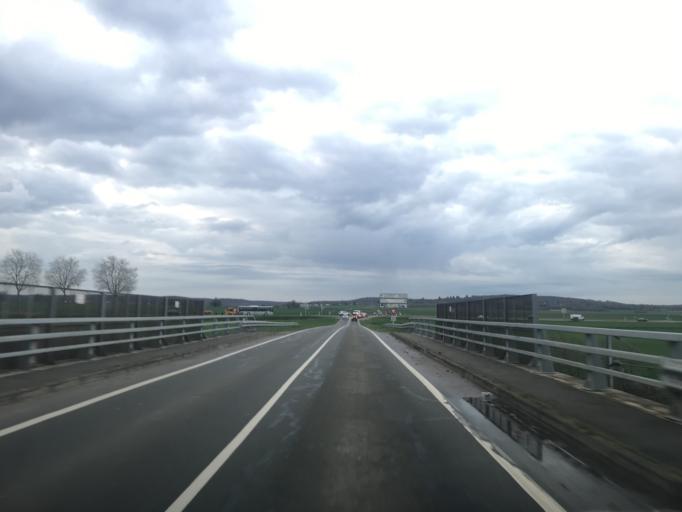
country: FR
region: Ile-de-France
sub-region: Departement des Yvelines
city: Villiers-Saint-Frederic
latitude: 48.8065
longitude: 1.8671
